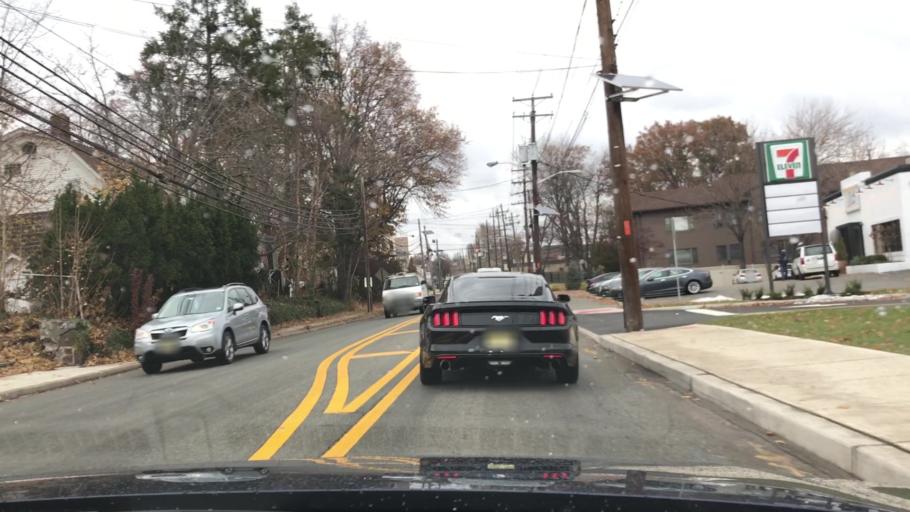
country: US
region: New Jersey
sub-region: Bergen County
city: East Rutherford
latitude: 40.8279
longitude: -74.0980
